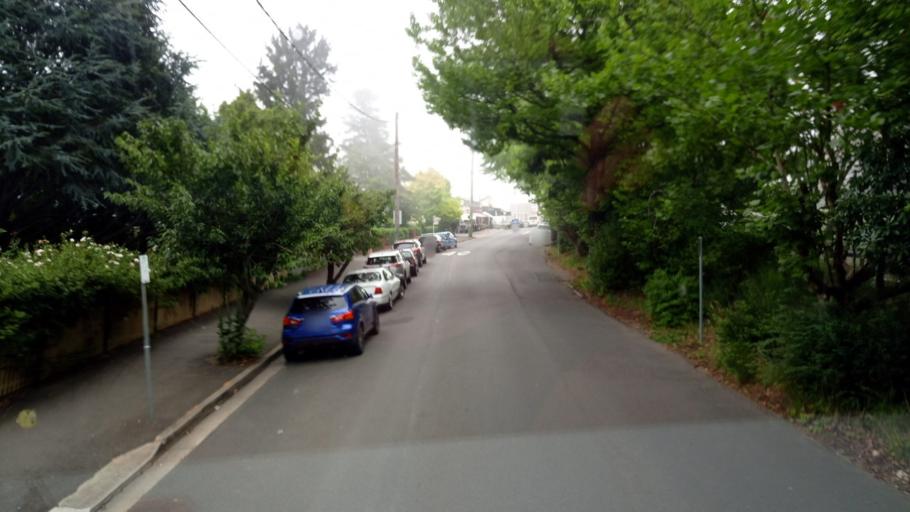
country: AU
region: New South Wales
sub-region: Blue Mountains Municipality
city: Leura
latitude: -33.7122
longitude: 150.3328
